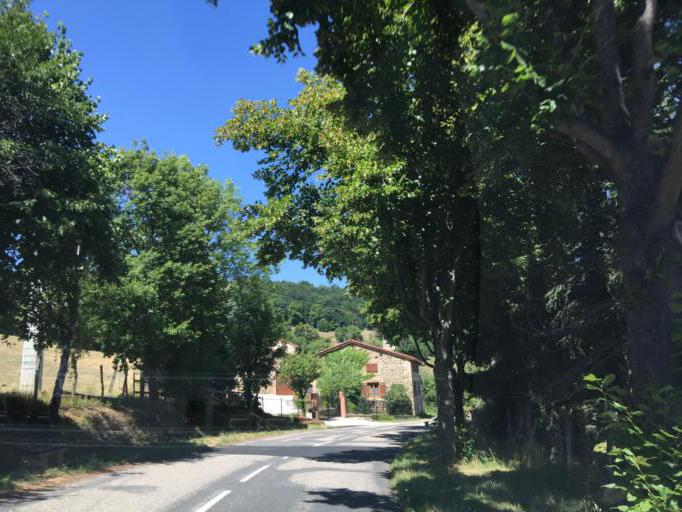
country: FR
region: Rhone-Alpes
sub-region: Departement de la Loire
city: Saint-Jean-Bonnefonds
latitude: 45.4565
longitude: 4.4494
